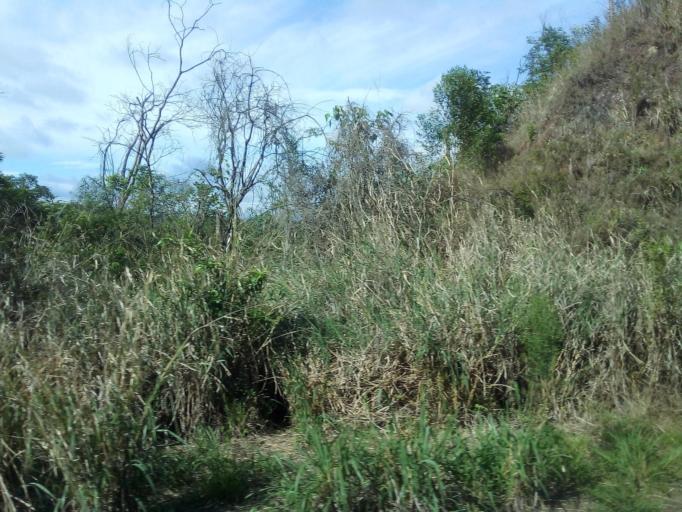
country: BR
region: Minas Gerais
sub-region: Caete
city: Caete
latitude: -19.8752
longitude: -43.7668
